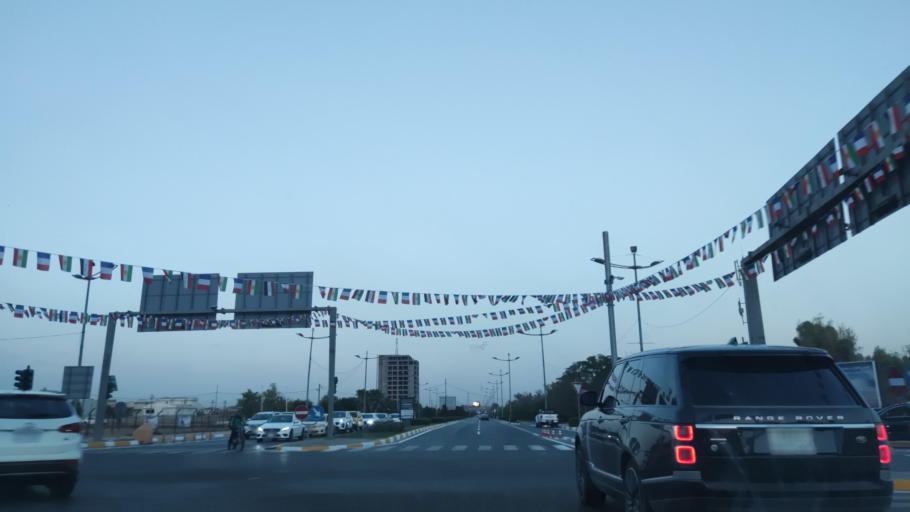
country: IQ
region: Arbil
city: Erbil
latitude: 36.1999
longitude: 43.9801
